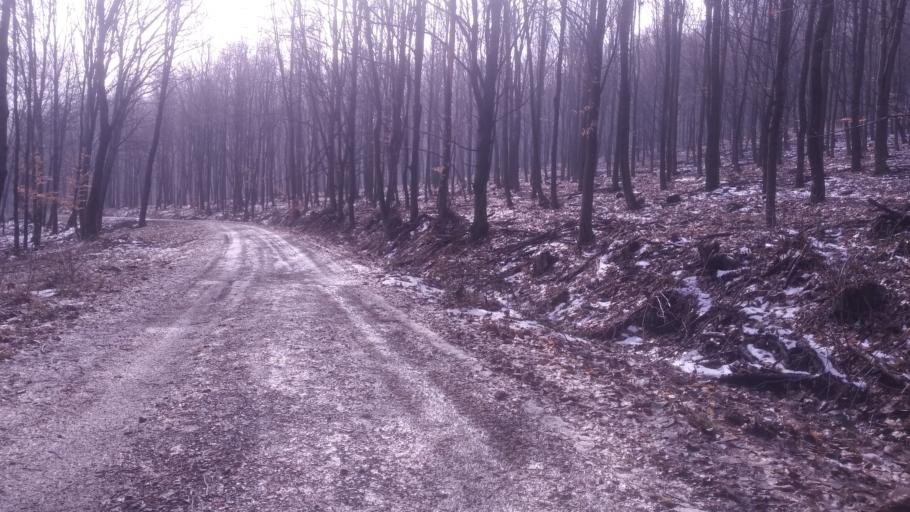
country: HU
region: Pest
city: Pilisszentkereszt
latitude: 47.7359
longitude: 18.9380
